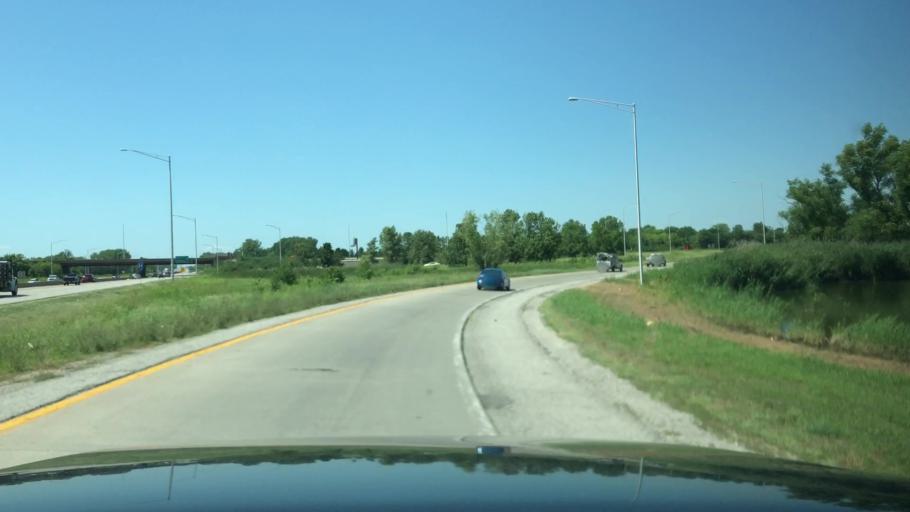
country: US
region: Illinois
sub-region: Saint Clair County
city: Alorton
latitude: 38.5801
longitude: -90.1047
